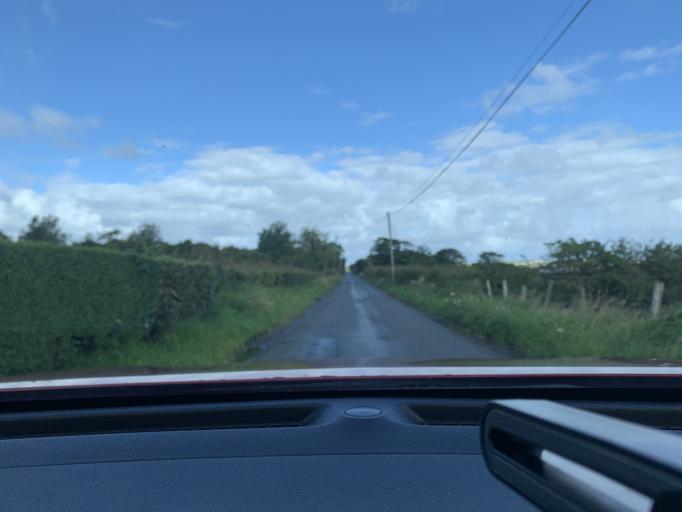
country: IE
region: Connaught
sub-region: Sligo
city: Strandhill
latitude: 54.3915
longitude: -8.5449
